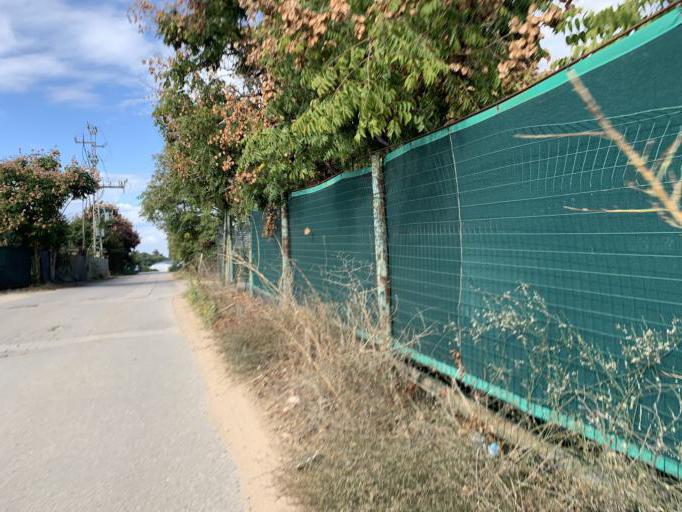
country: IL
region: Central District
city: Hod HaSharon
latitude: 32.1674
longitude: 34.8799
